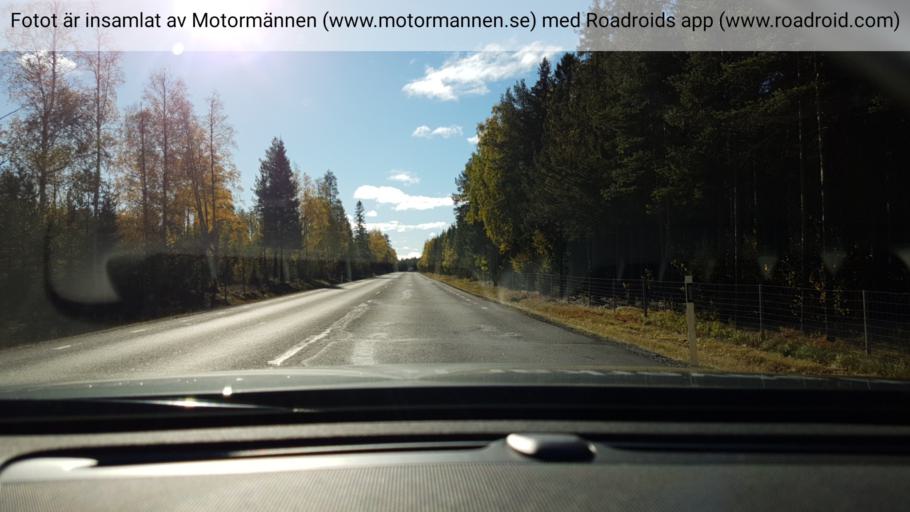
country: SE
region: Vaesterbotten
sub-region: Skelleftea Kommun
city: Burea
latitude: 64.5753
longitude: 21.2237
